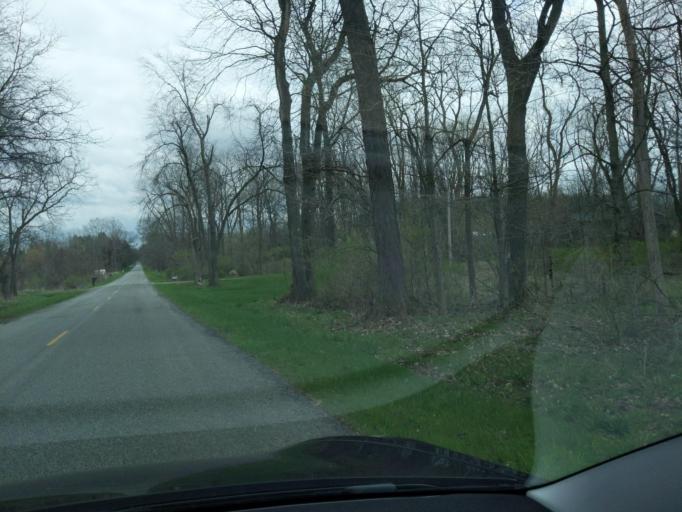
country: US
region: Michigan
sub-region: Ingham County
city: Holt
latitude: 42.5676
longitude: -84.5760
